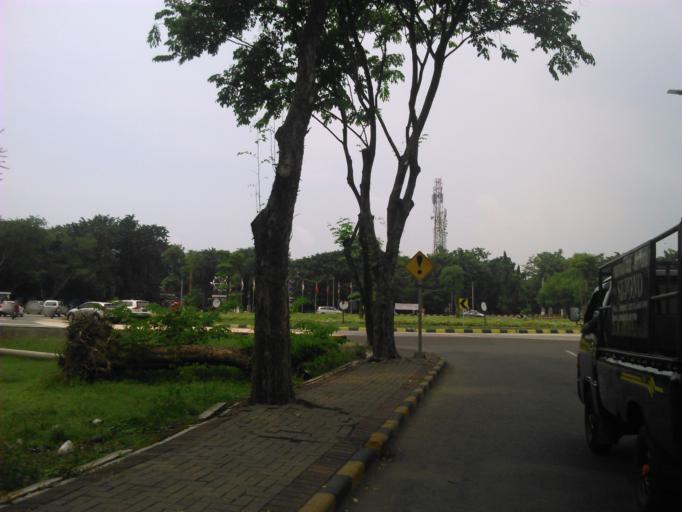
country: ID
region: East Java
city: Mulyorejo
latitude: -7.2785
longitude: 112.7903
